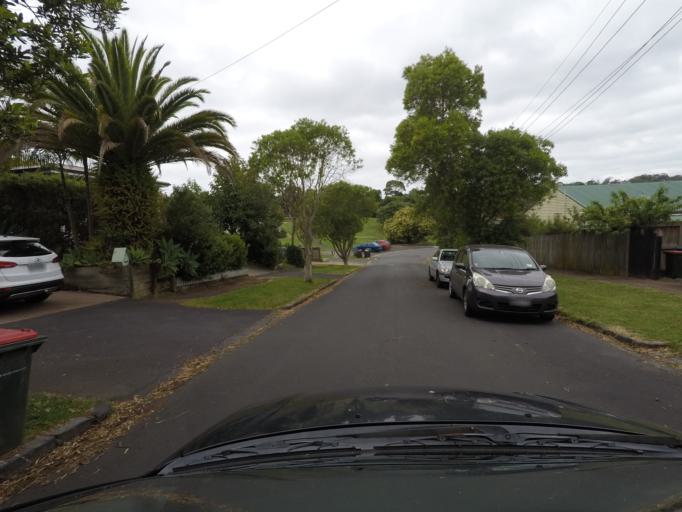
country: NZ
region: Auckland
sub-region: Auckland
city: Auckland
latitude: -36.8669
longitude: 174.7363
